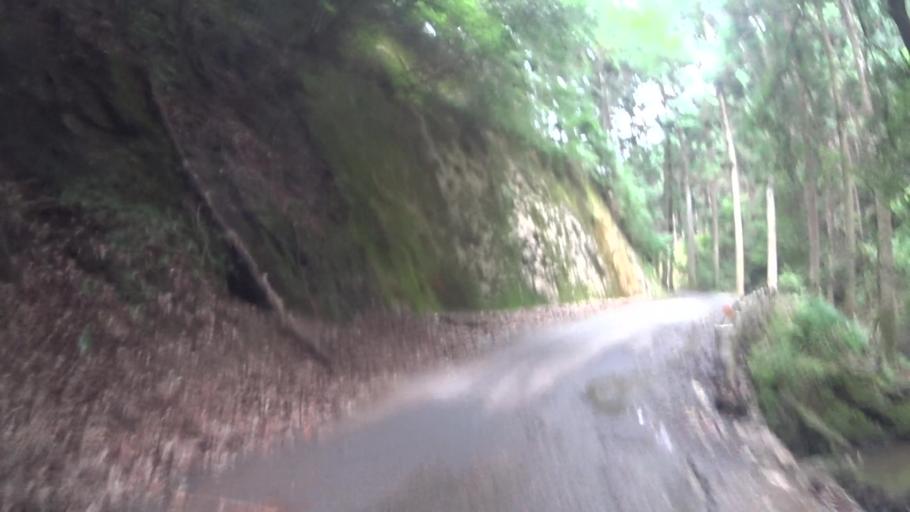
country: JP
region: Kyoto
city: Kameoka
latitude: 35.1571
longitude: 135.5730
